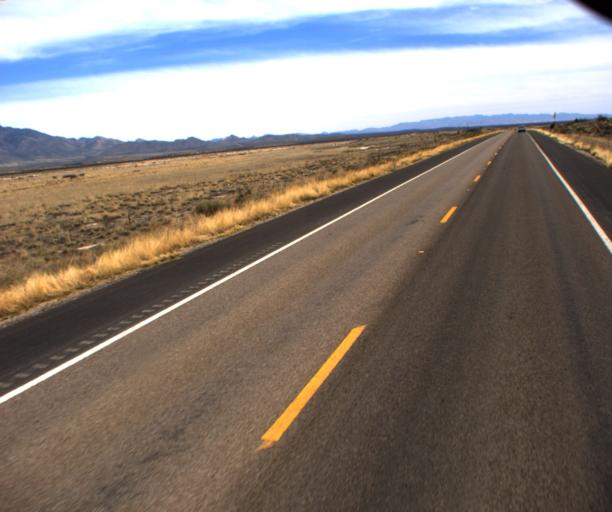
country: US
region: Arizona
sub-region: Cochise County
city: Willcox
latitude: 32.2196
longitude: -109.7885
